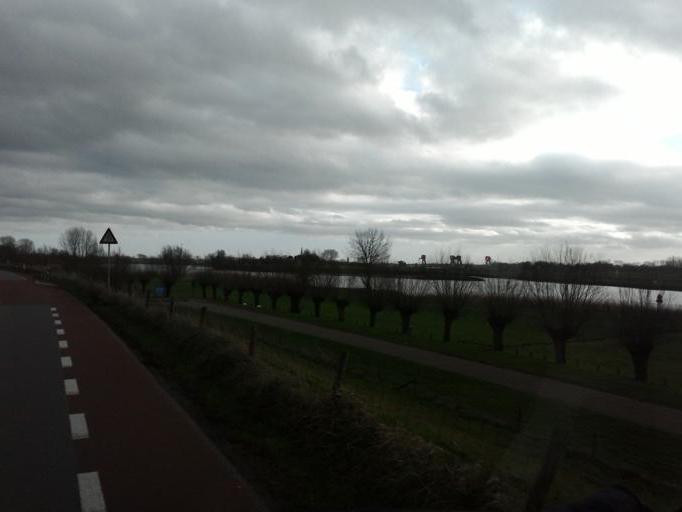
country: NL
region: Utrecht
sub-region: Gemeente Vianen
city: Vianen
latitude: 51.9996
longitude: 5.1284
